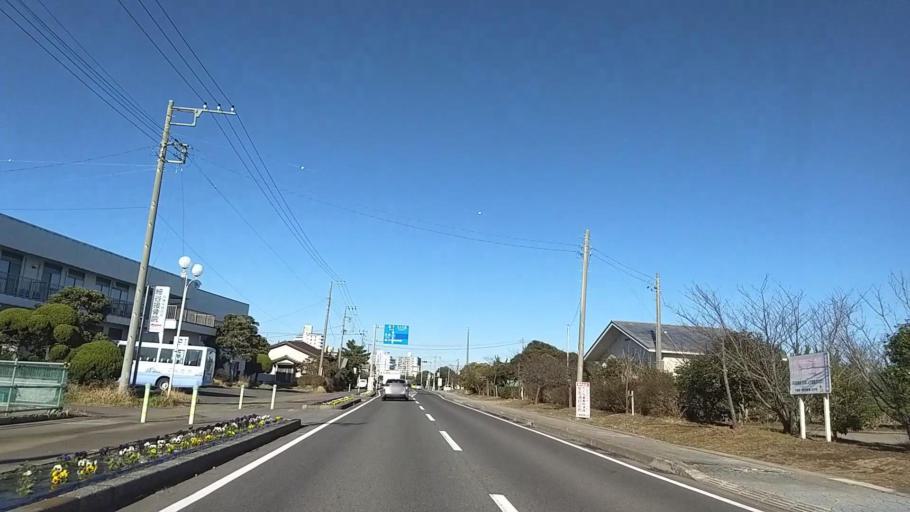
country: JP
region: Chiba
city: Mobara
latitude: 35.4436
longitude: 140.4004
